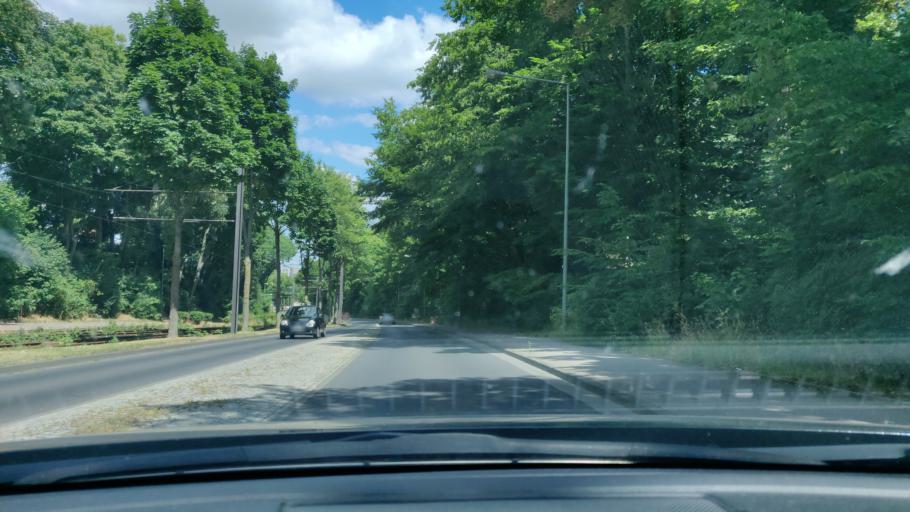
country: DE
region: Hesse
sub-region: Regierungsbezirk Kassel
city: Baunatal
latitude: 51.2695
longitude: 9.4386
